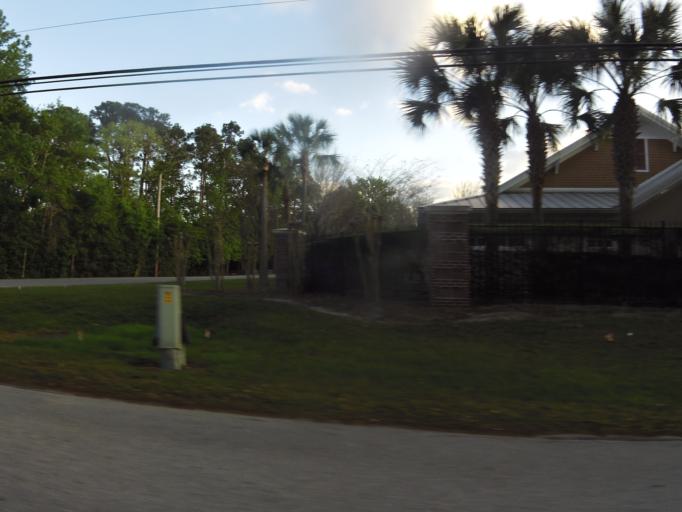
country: US
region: Florida
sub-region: Saint Johns County
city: Fruit Cove
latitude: 30.1256
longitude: -81.6211
